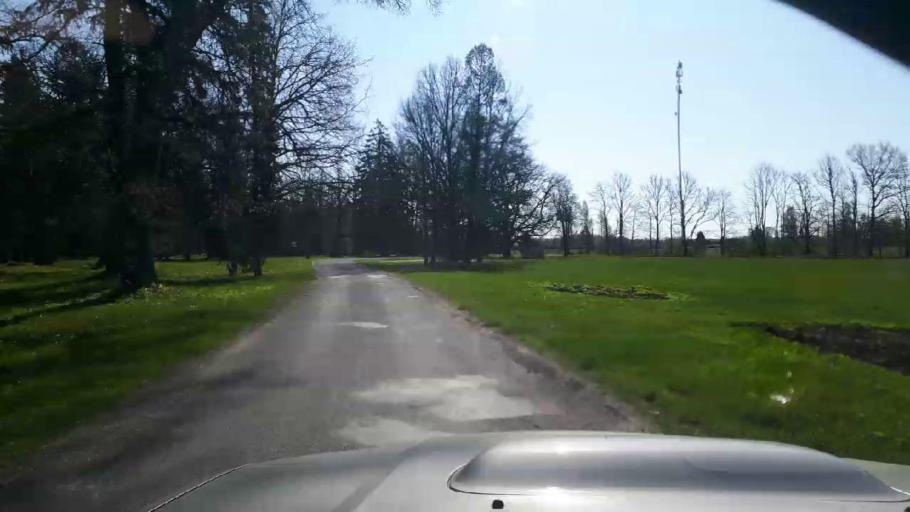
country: EE
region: Paernumaa
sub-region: Sindi linn
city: Sindi
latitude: 58.4505
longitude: 24.7651
